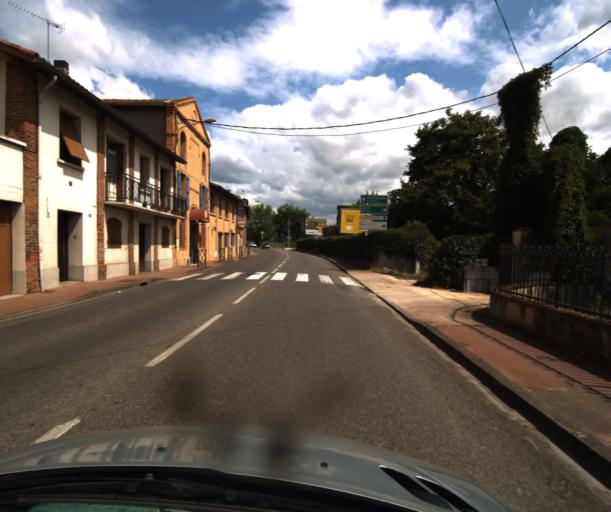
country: FR
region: Midi-Pyrenees
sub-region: Departement du Tarn-et-Garonne
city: Montauban
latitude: 44.0103
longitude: 1.3493
